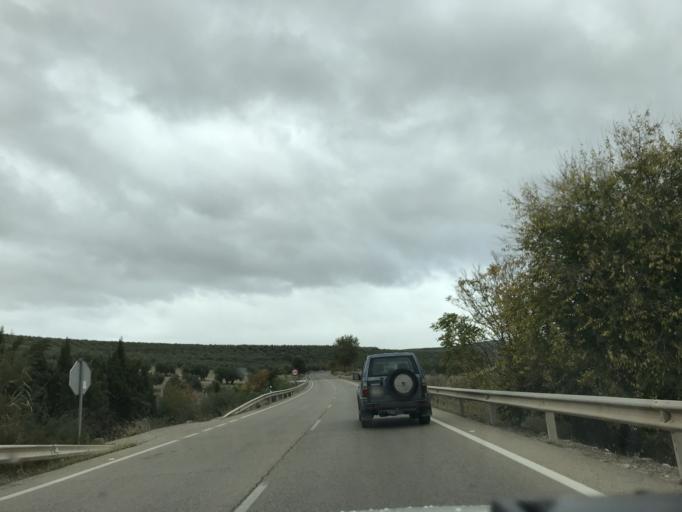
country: ES
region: Andalusia
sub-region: Provincia de Jaen
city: Peal de Becerro
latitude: 37.9250
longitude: -3.1375
